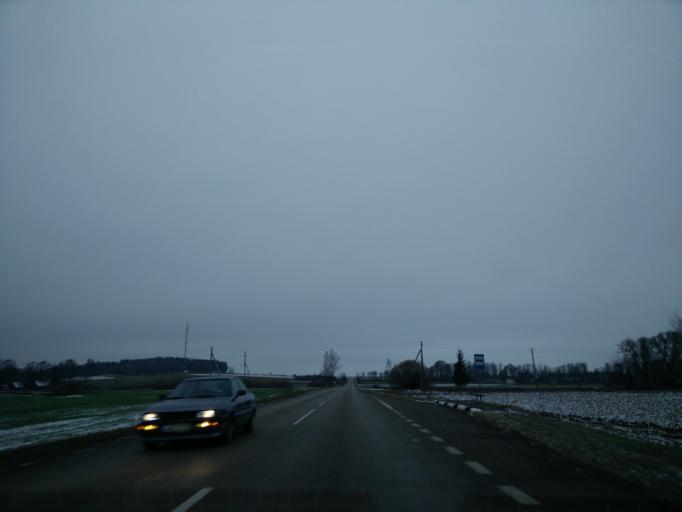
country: LT
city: Ariogala
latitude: 55.3411
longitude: 23.3960
